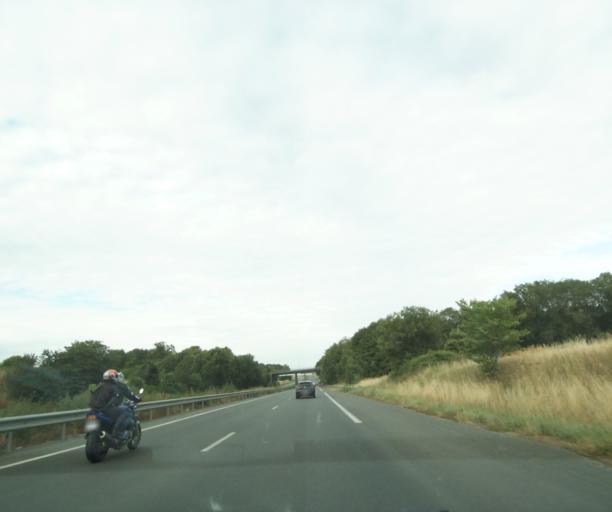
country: FR
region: Poitou-Charentes
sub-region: Departement de la Charente-Maritime
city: Dompierre-sur-Mer
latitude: 46.1960
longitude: -1.0560
